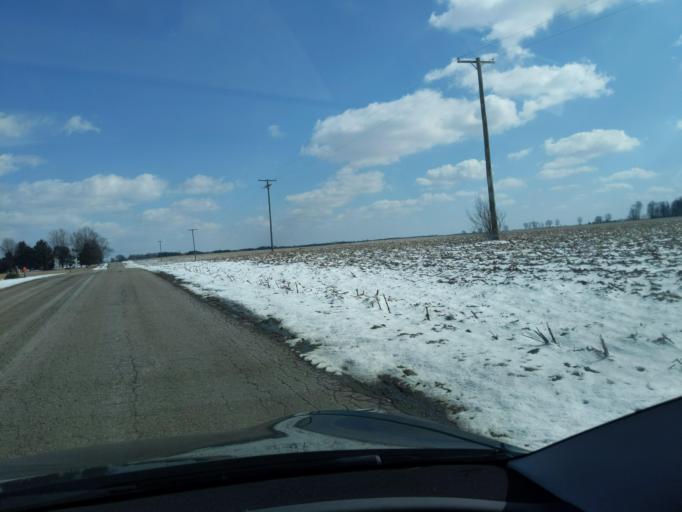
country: US
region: Michigan
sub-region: Ingham County
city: Williamston
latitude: 42.6155
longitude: -84.2955
